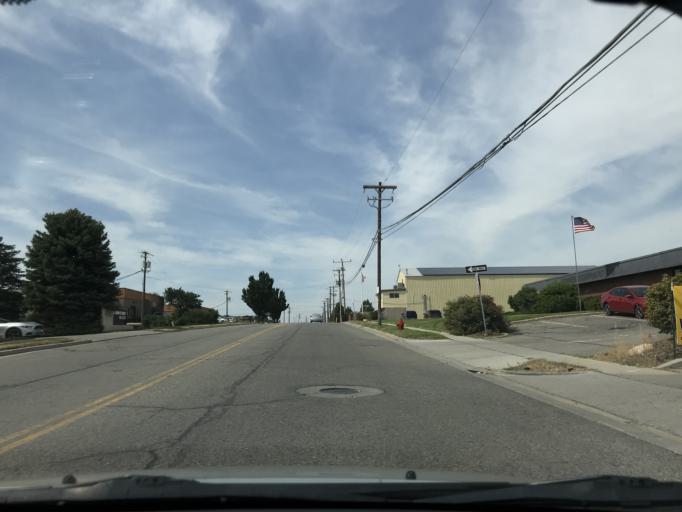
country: US
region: Utah
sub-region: Salt Lake County
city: Centerfield
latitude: 40.6830
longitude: -111.9055
